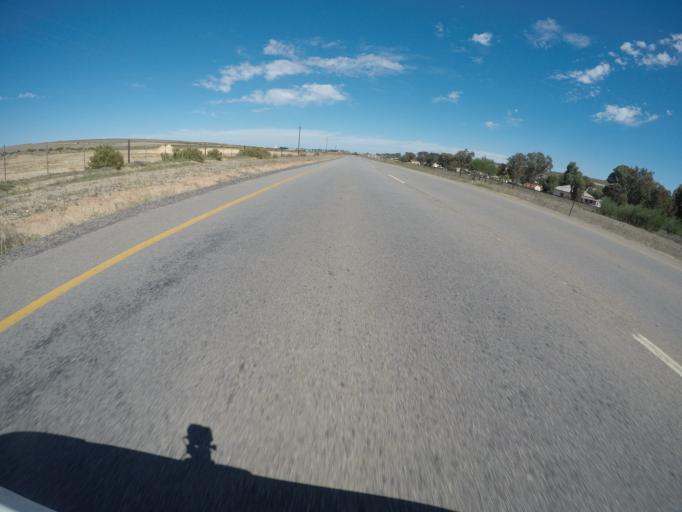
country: ZA
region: Western Cape
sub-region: West Coast District Municipality
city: Malmesbury
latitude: -33.4895
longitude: 18.6855
